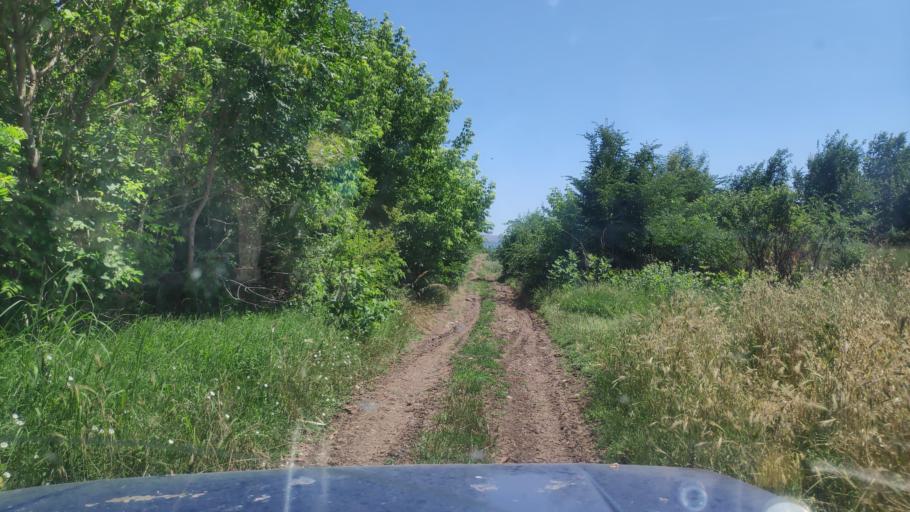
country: MK
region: Kumanovo
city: Bedinje
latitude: 42.1692
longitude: 21.6869
